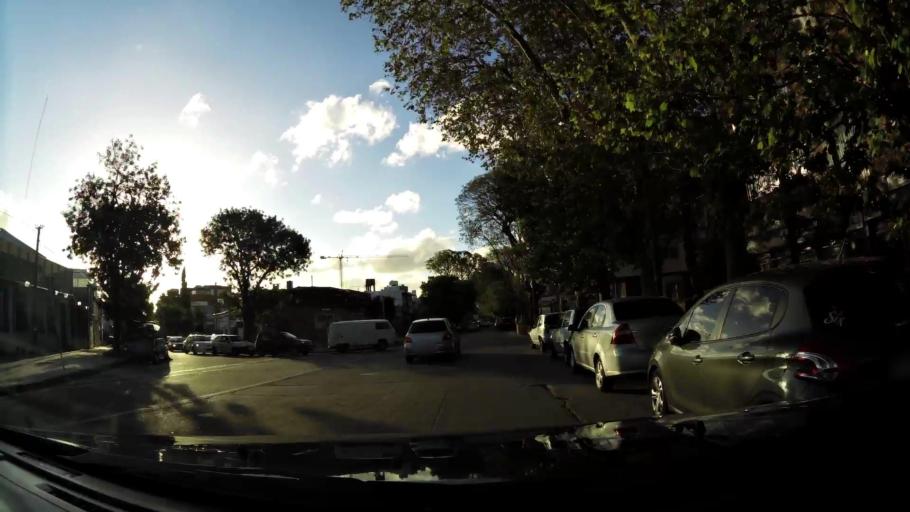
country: UY
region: Montevideo
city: Montevideo
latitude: -34.8853
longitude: -56.1480
